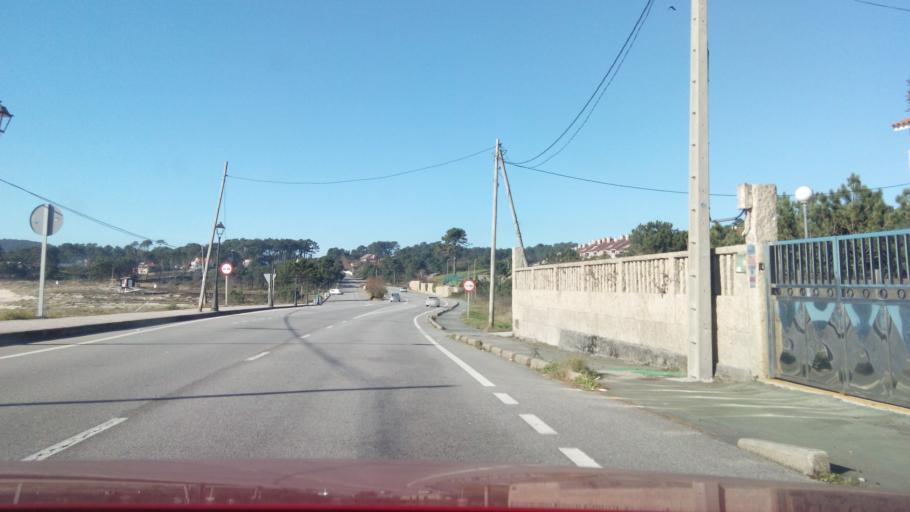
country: ES
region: Galicia
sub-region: Provincia de Pontevedra
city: O Grove
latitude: 42.4609
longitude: -8.8953
